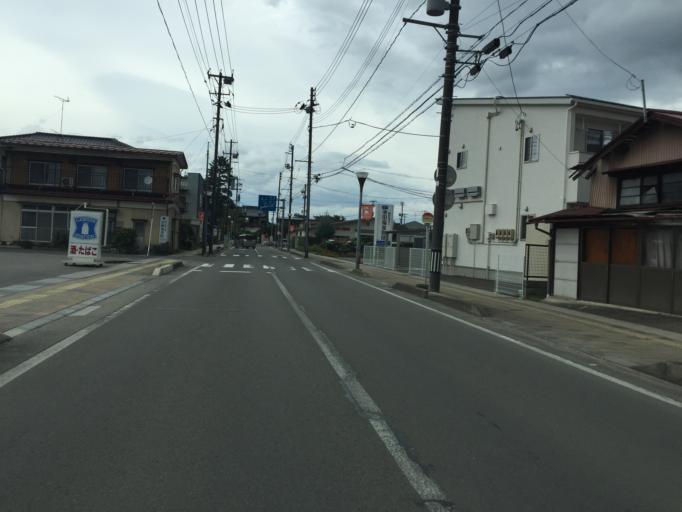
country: JP
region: Fukushima
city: Hobaramachi
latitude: 37.8255
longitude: 140.5551
